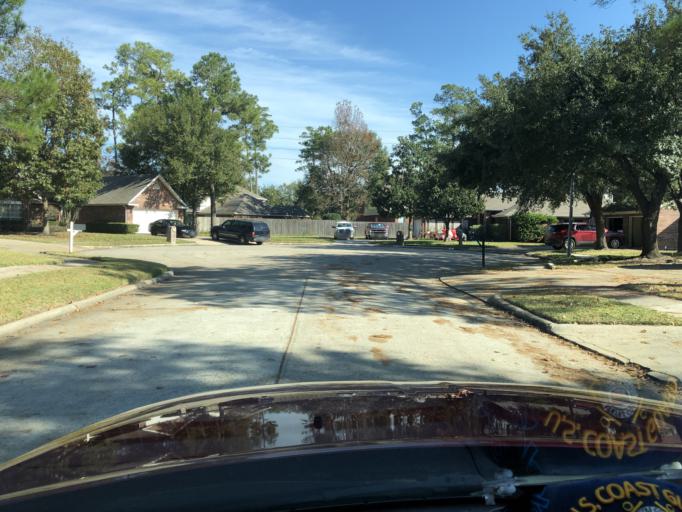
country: US
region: Texas
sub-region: Harris County
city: Tomball
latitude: 30.0217
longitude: -95.5583
